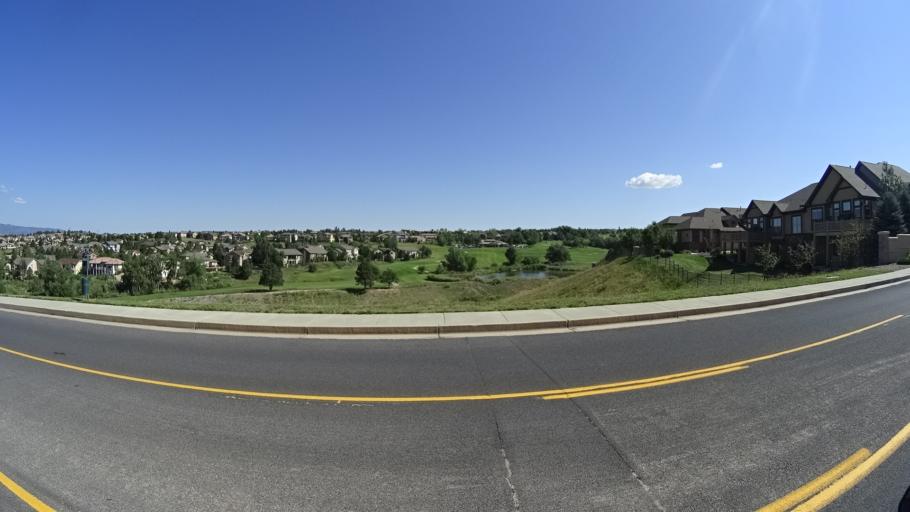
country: US
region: Colorado
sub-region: El Paso County
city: Air Force Academy
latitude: 38.9691
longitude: -104.7785
